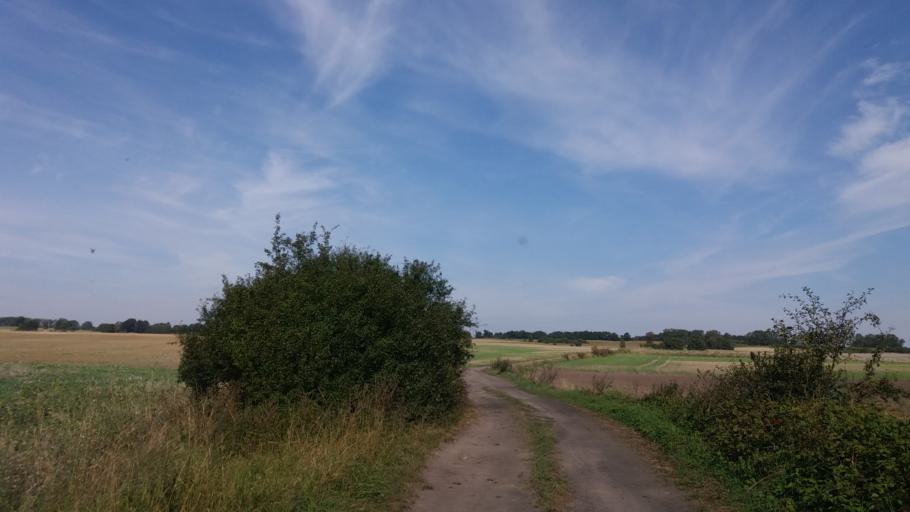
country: PL
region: West Pomeranian Voivodeship
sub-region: Powiat choszczenski
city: Choszczno
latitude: 53.1108
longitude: 15.4103
